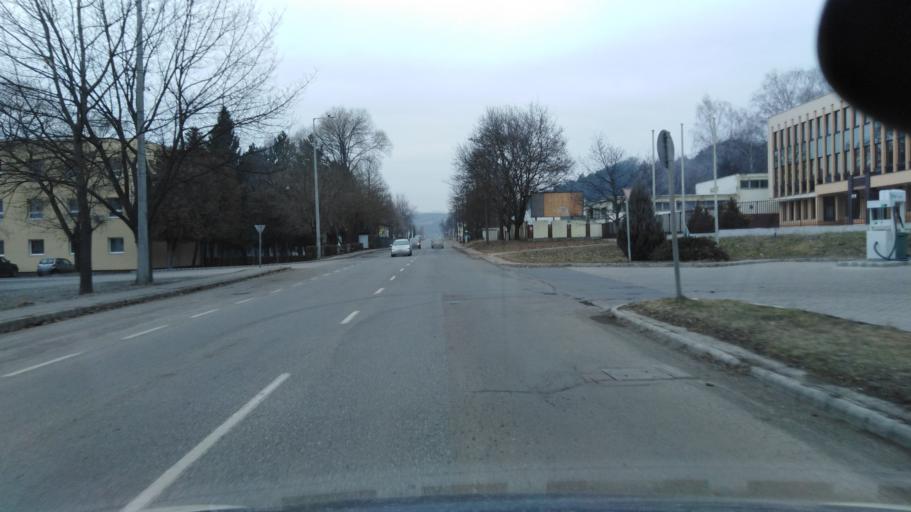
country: HU
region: Nograd
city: Salgotarjan
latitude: 48.0814
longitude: 19.7934
